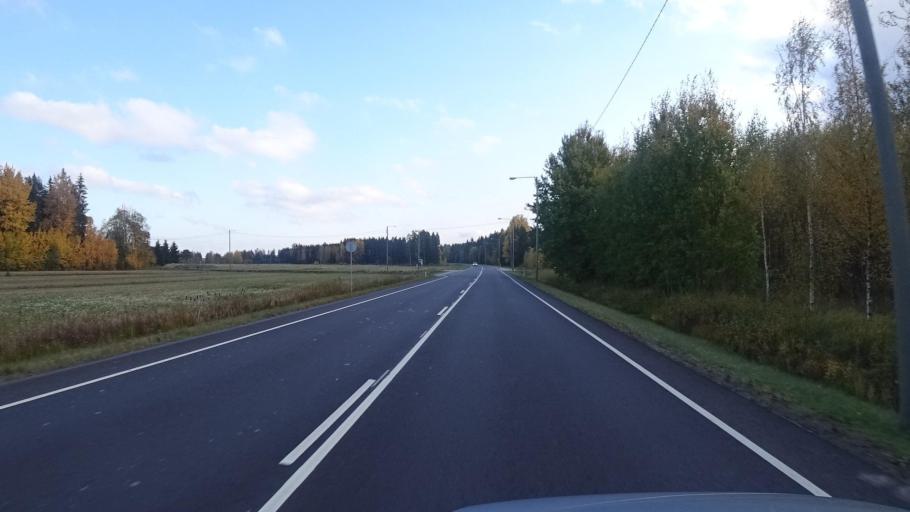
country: FI
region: Satakunta
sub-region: Rauma
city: Koeylioe
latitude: 61.0976
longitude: 22.2373
